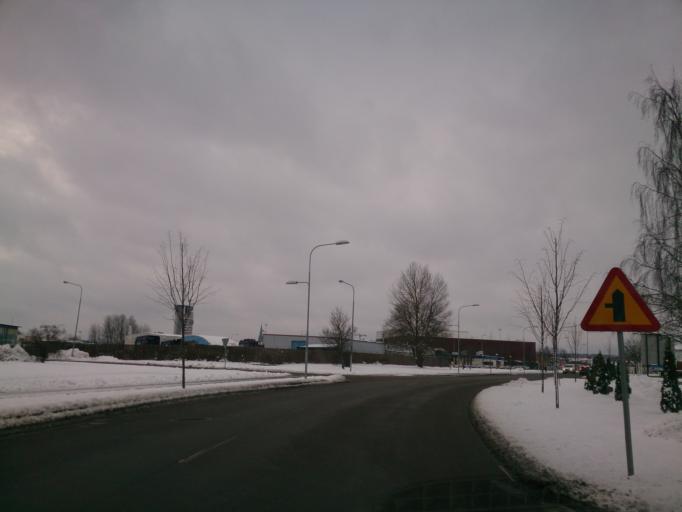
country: SE
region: OEstergoetland
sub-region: Linkopings Kommun
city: Linkoping
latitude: 58.4291
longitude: 15.6131
